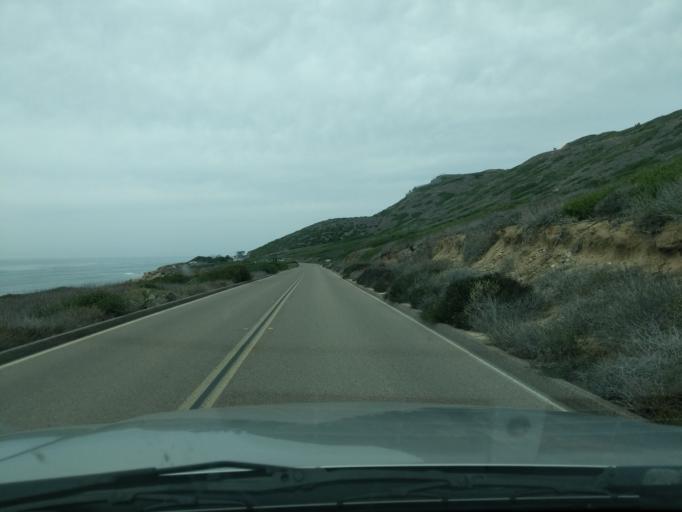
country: US
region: California
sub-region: San Diego County
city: Coronado
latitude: 32.6721
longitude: -117.2441
